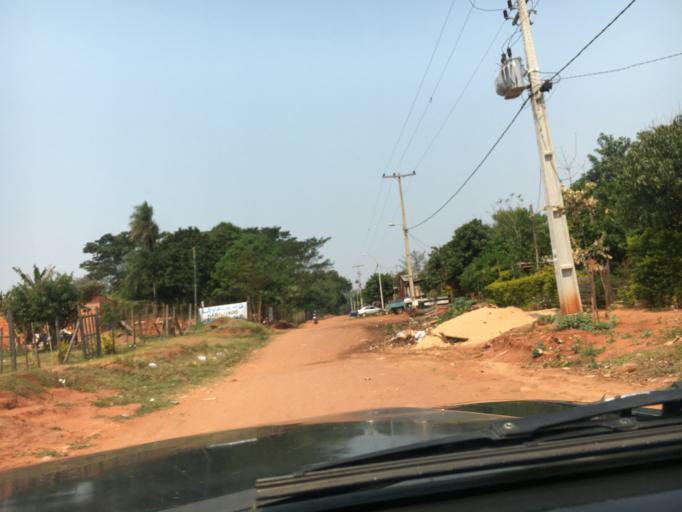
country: PY
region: Central
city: Villa Elisa
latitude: -25.3850
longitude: -57.5691
